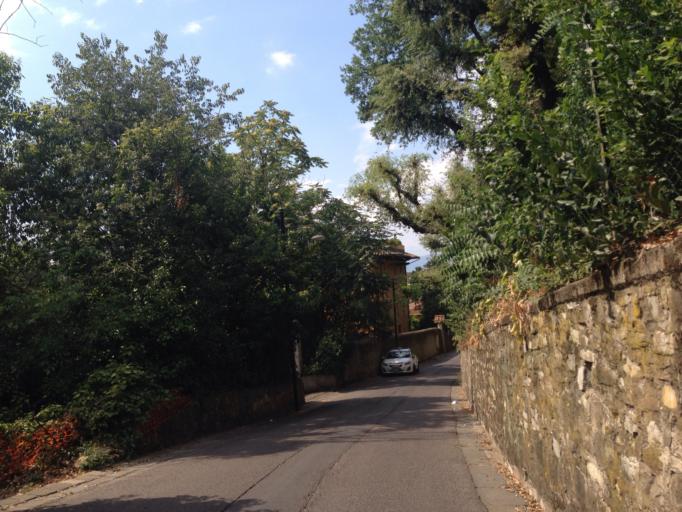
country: IT
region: Tuscany
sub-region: Province of Florence
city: Florence
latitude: 43.7614
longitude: 11.2636
